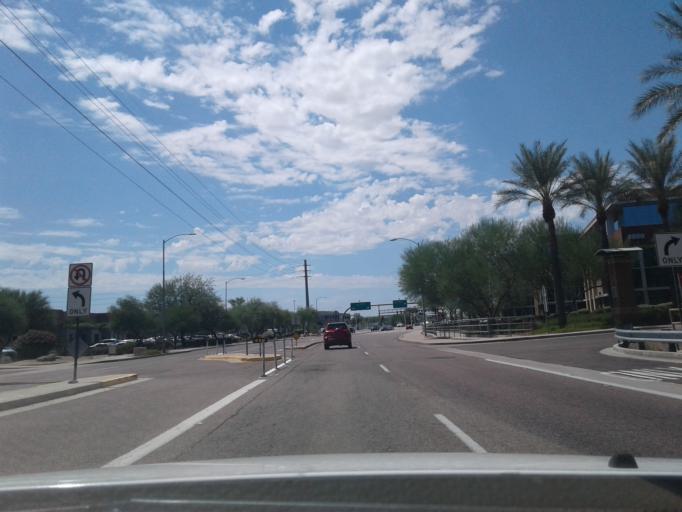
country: US
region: Arizona
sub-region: Maricopa County
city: Paradise Valley
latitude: 33.6186
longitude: -111.8883
